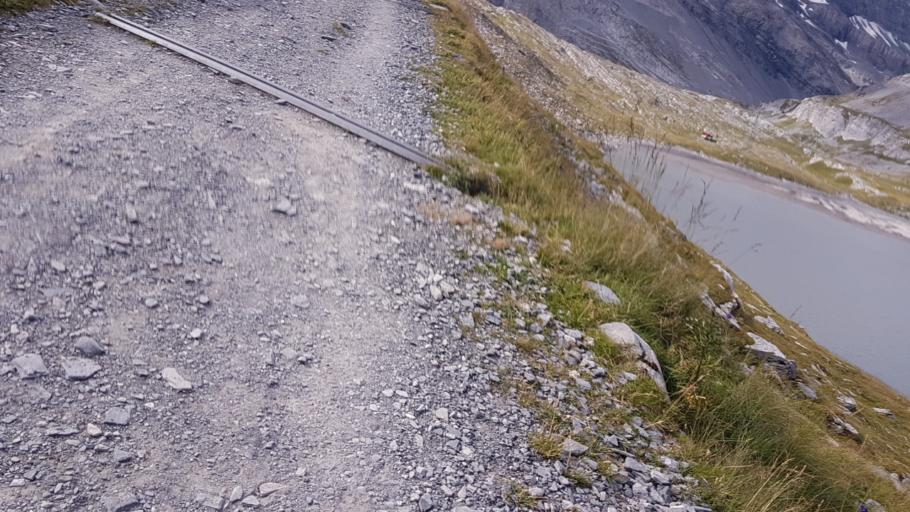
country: CH
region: Valais
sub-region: Leuk District
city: Leukerbad
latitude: 46.4094
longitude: 7.6221
